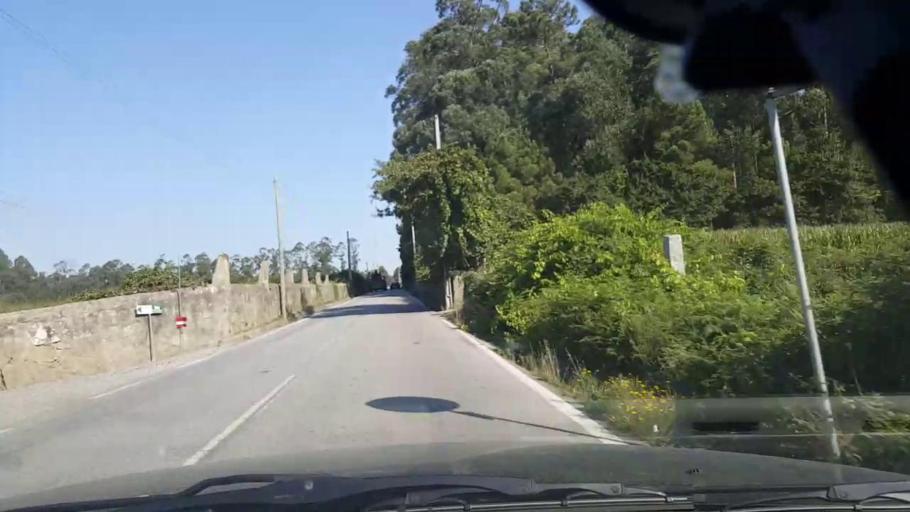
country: PT
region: Porto
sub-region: Vila do Conde
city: Arvore
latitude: 41.3165
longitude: -8.6791
